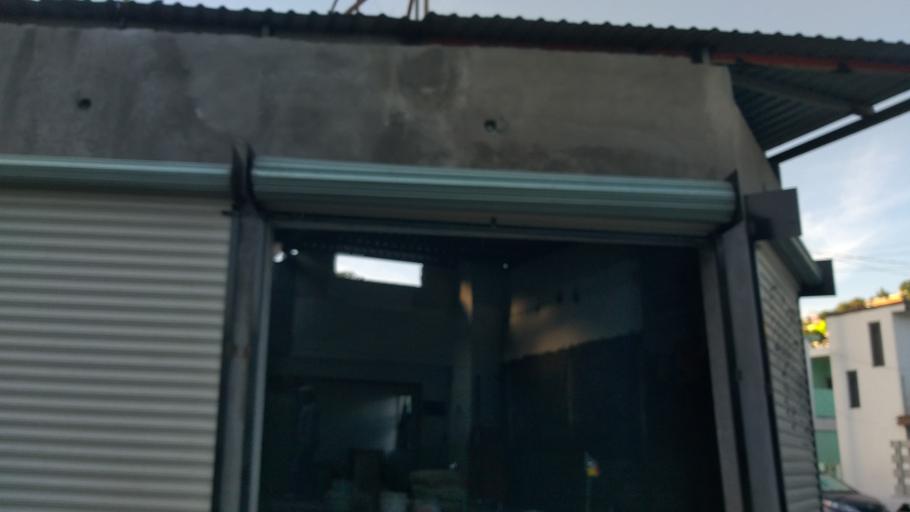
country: MX
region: Nuevo Leon
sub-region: Monterrey
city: Monterrey
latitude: 25.6386
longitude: -100.3081
